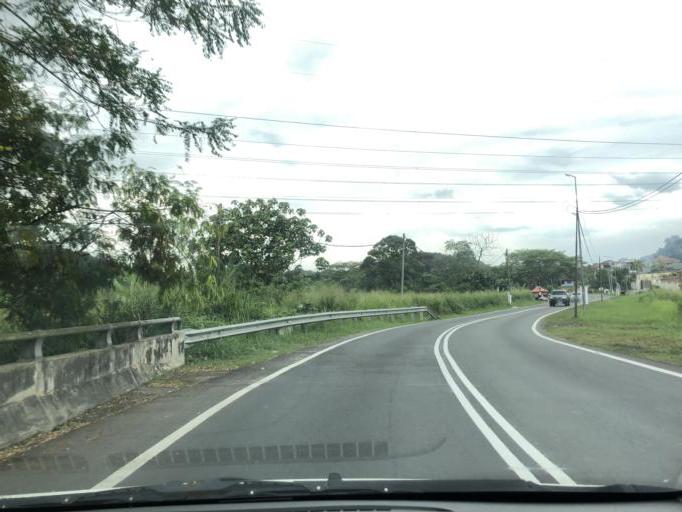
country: MY
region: Putrajaya
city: Putrajaya
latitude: 2.9179
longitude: 101.7540
